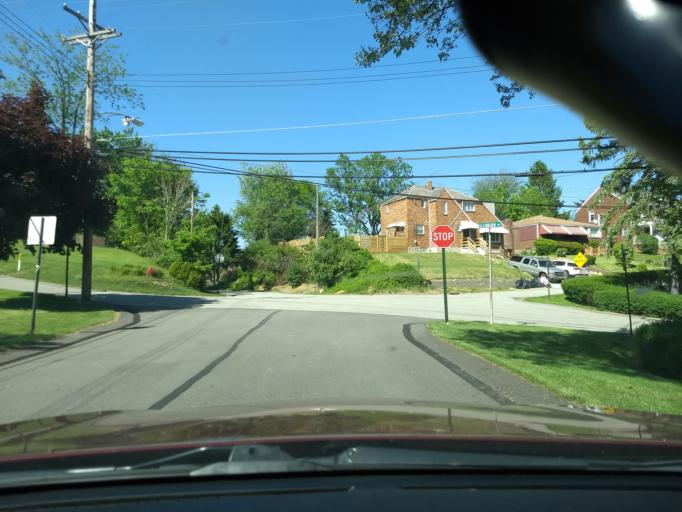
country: US
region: Pennsylvania
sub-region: Allegheny County
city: Pleasant Hills
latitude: 40.3428
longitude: -79.9613
